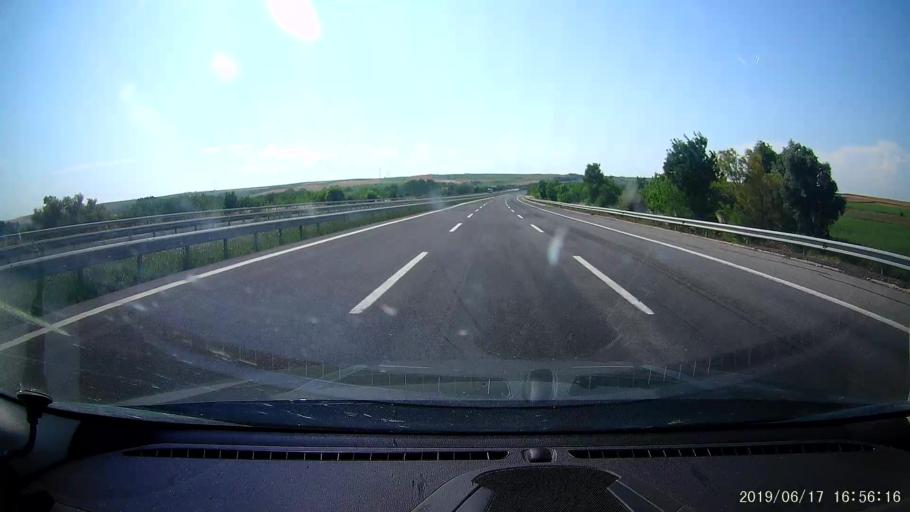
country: TR
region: Edirne
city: Haskoy
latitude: 41.5852
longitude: 26.9414
